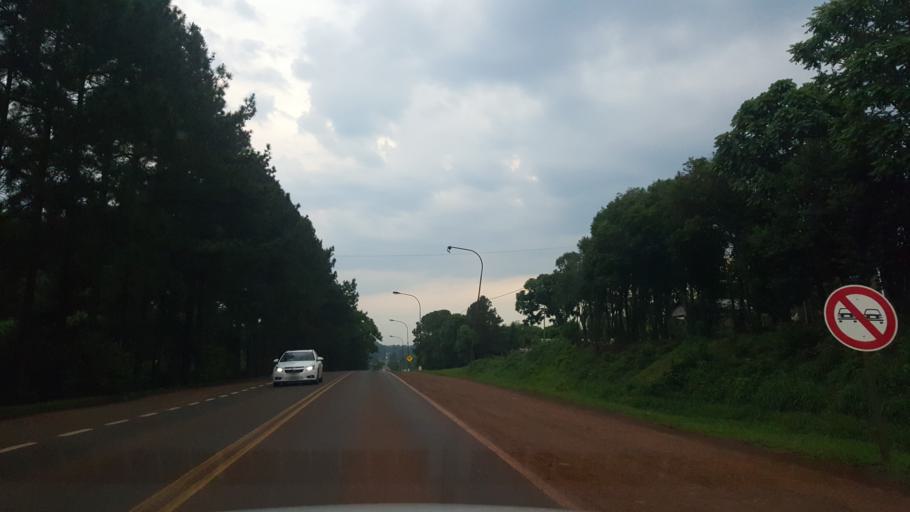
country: AR
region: Misiones
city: Gobernador Roca
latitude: -27.1813
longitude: -55.4591
